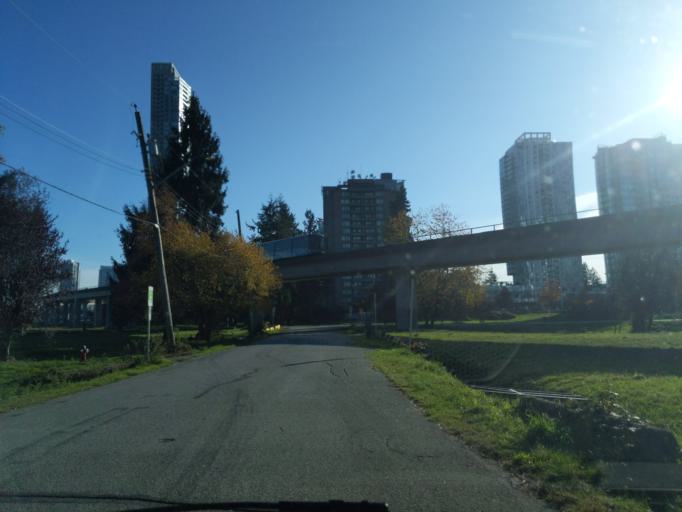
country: CA
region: British Columbia
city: New Westminster
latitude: 49.1940
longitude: -122.8495
